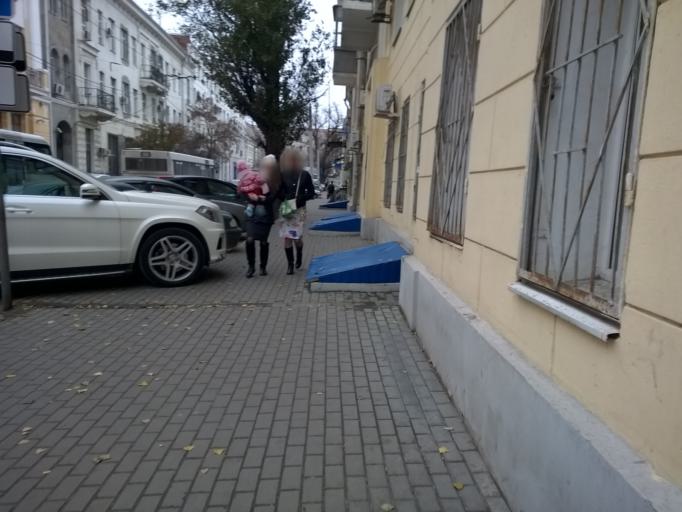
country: RU
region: Rostov
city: Rostov-na-Donu
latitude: 47.2190
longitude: 39.7170
